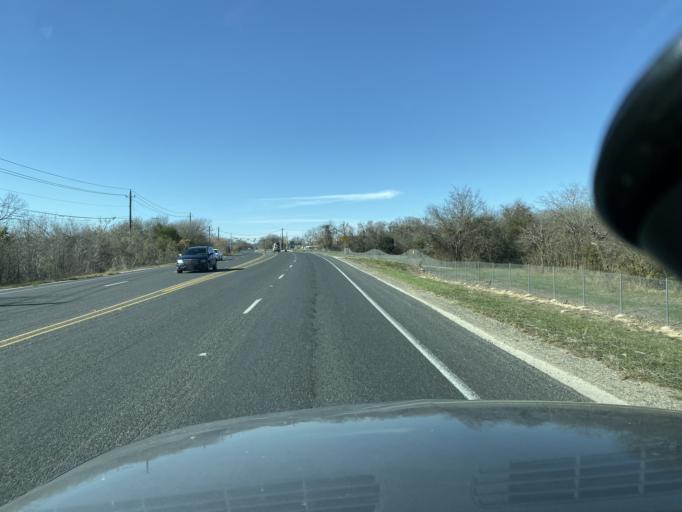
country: US
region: Texas
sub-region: Travis County
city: Garfield
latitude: 30.1723
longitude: -97.6681
